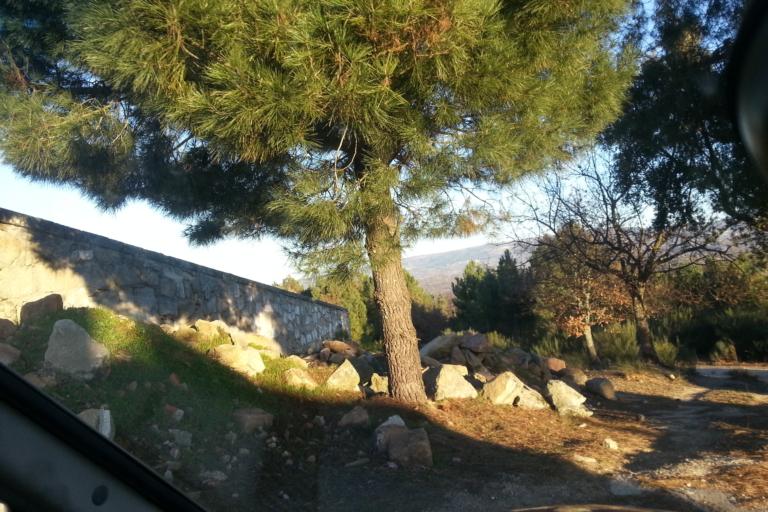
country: PT
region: Guarda
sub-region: Fornos de Algodres
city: Fornos de Algodres
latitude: 40.6076
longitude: -7.5004
